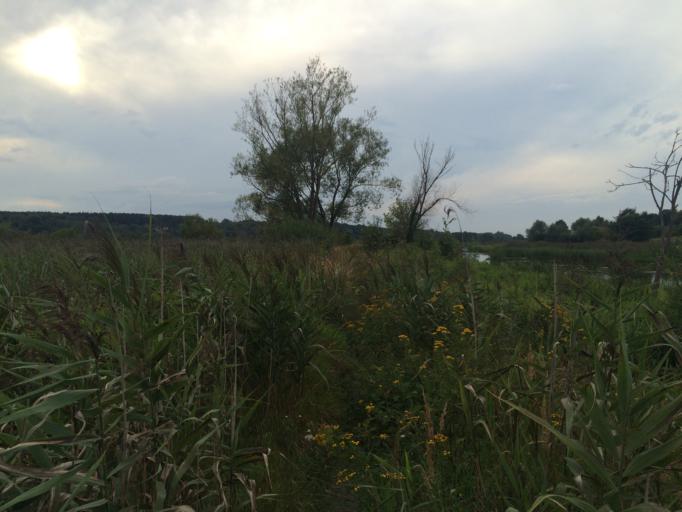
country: PL
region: Swietokrzyskie
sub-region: Powiat starachowicki
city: Starachowice
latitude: 51.0522
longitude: 21.0525
